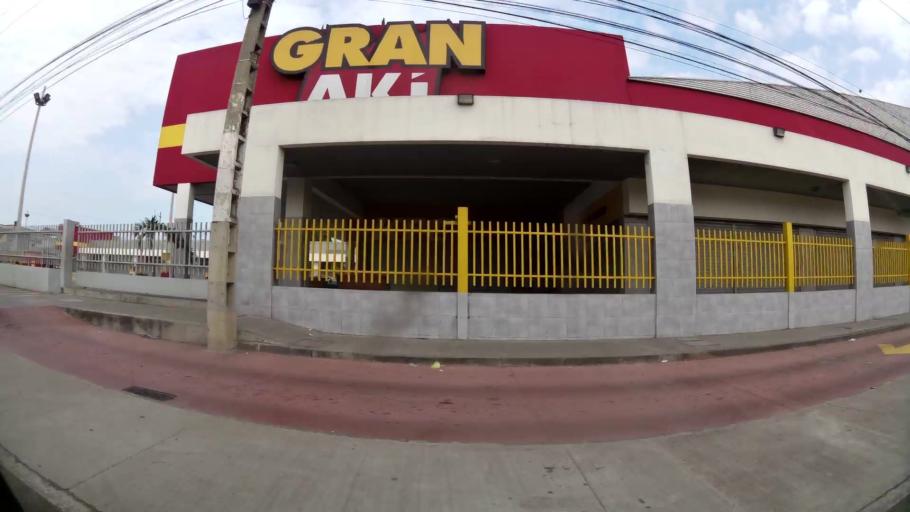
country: EC
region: Guayas
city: Guayaquil
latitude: -2.2419
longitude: -79.8911
